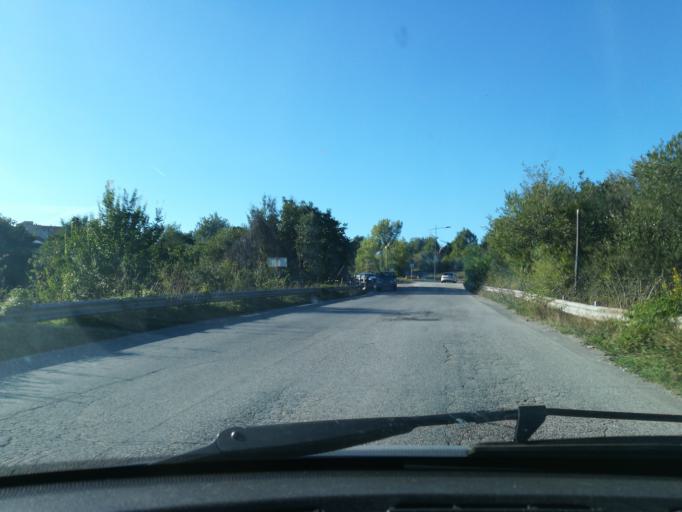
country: IT
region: The Marches
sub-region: Provincia di Macerata
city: Tolentino
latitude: 43.2134
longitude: 13.3067
